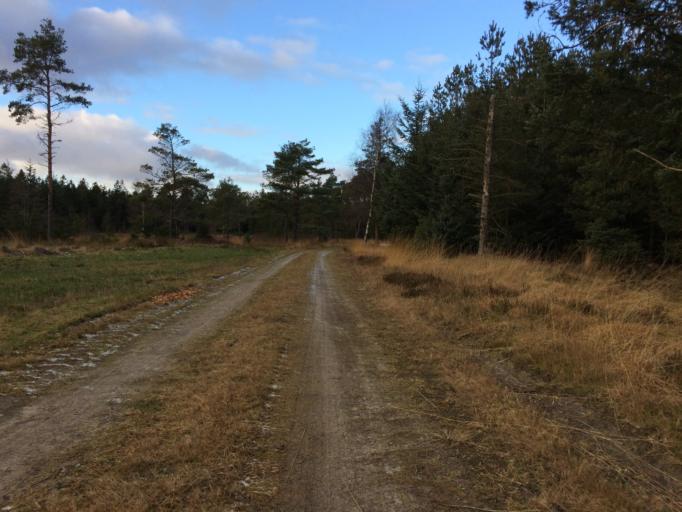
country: DK
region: Central Jutland
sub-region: Holstebro Kommune
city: Ulfborg
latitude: 56.2658
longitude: 8.3922
